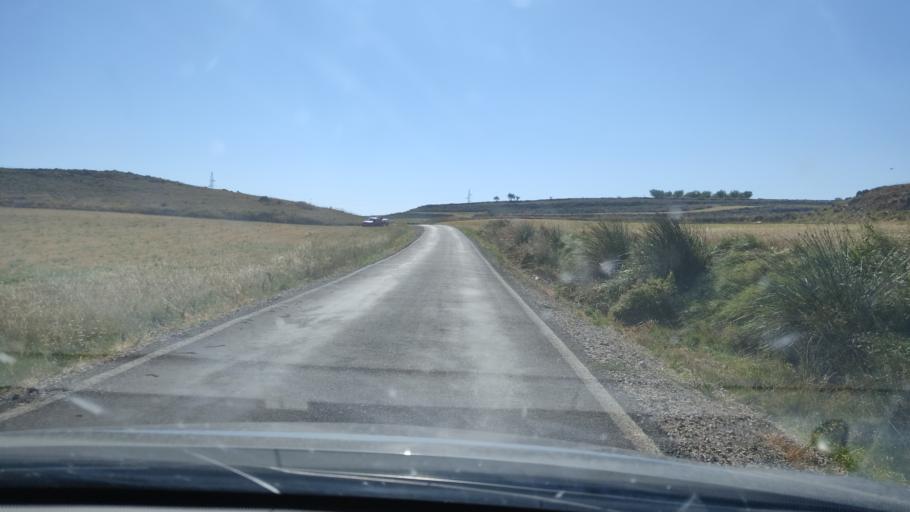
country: ES
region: Aragon
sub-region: Provincia de Teruel
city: Monforte de Moyuela
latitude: 41.0430
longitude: -0.9947
